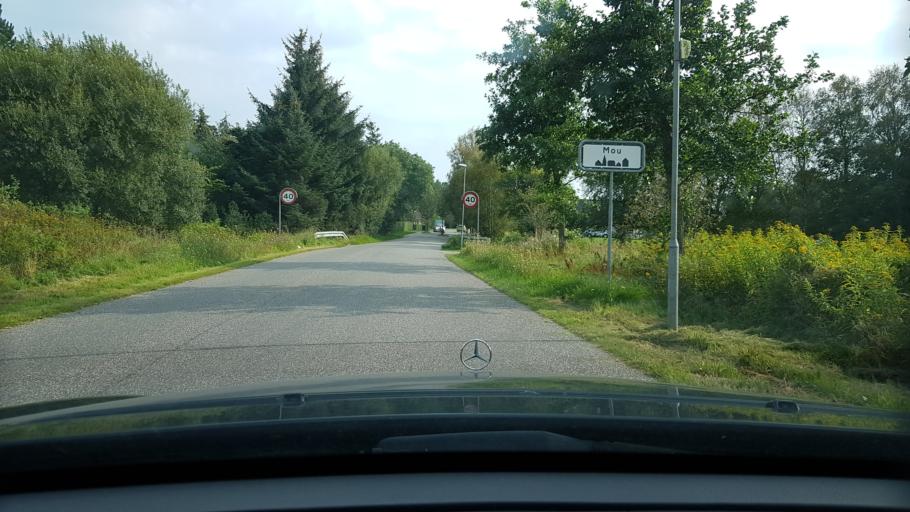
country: DK
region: North Denmark
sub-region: Alborg Kommune
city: Hals
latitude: 56.9751
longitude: 10.2159
